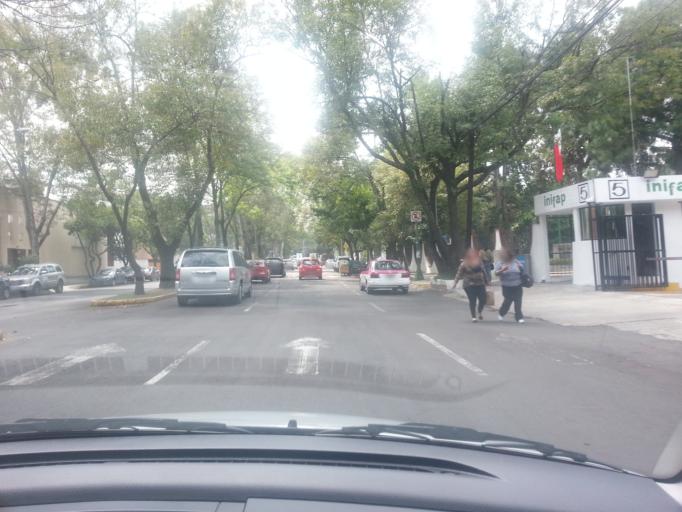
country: MX
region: Mexico City
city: Coyoacan
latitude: 19.3513
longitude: -99.1749
